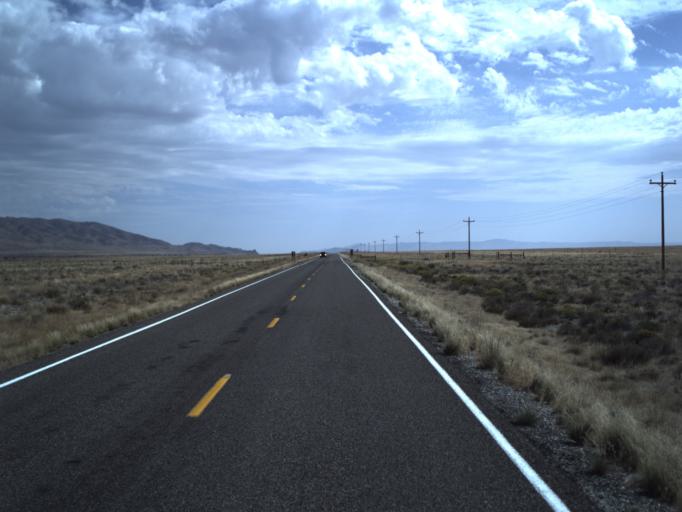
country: US
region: Utah
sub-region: Tooele County
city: Wendover
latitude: 41.4297
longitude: -113.8114
